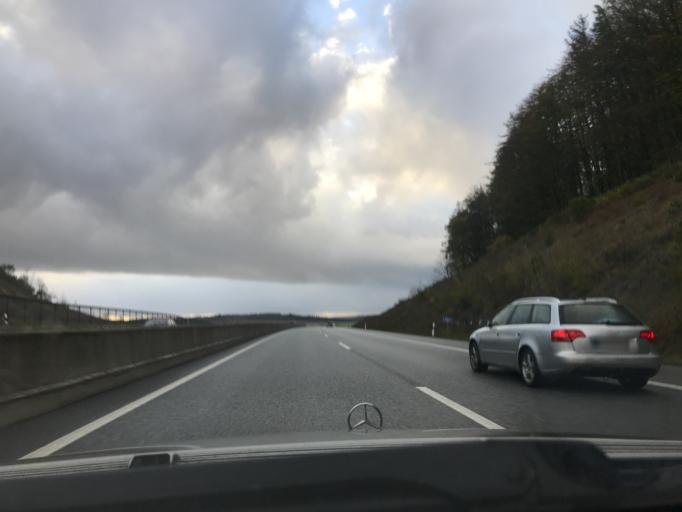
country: DE
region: Thuringia
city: Sollstedt
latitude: 51.4224
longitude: 10.5172
